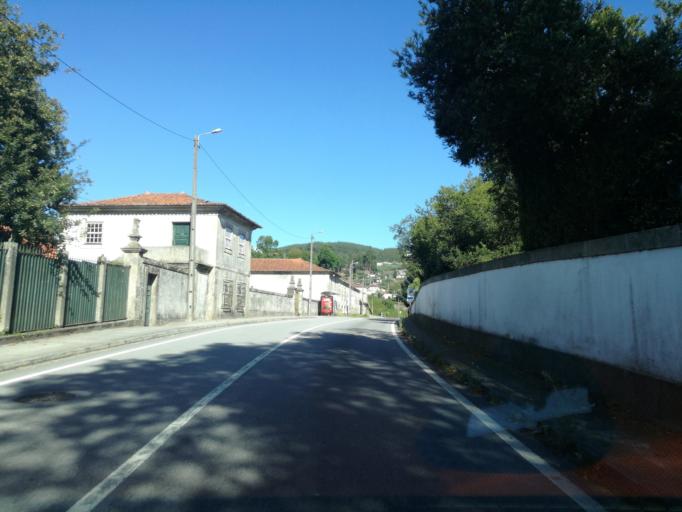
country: PT
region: Porto
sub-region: Pacos de Ferreira
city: Seroa
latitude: 41.2570
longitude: -8.4703
